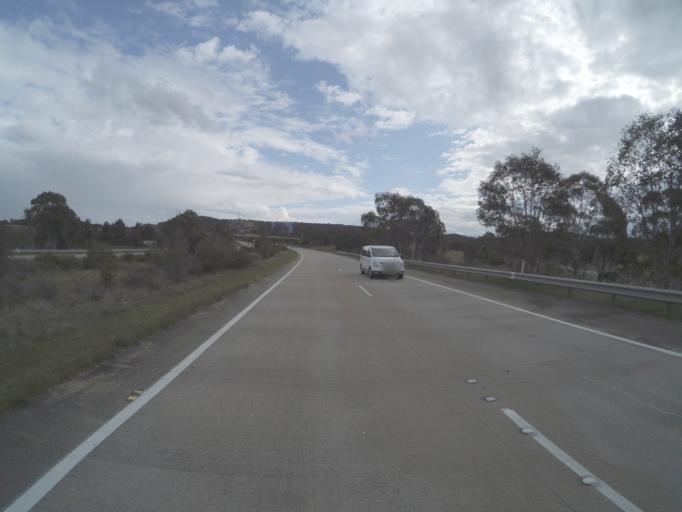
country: AU
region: New South Wales
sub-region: Goulburn Mulwaree
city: Goulburn
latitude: -34.7406
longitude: 149.7740
